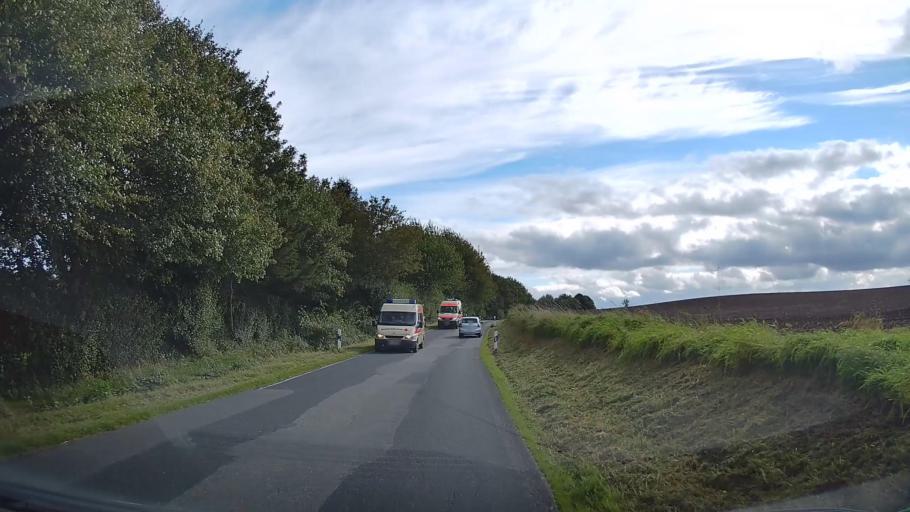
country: DE
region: Schleswig-Holstein
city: Ringsberg
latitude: 54.8372
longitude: 9.5889
